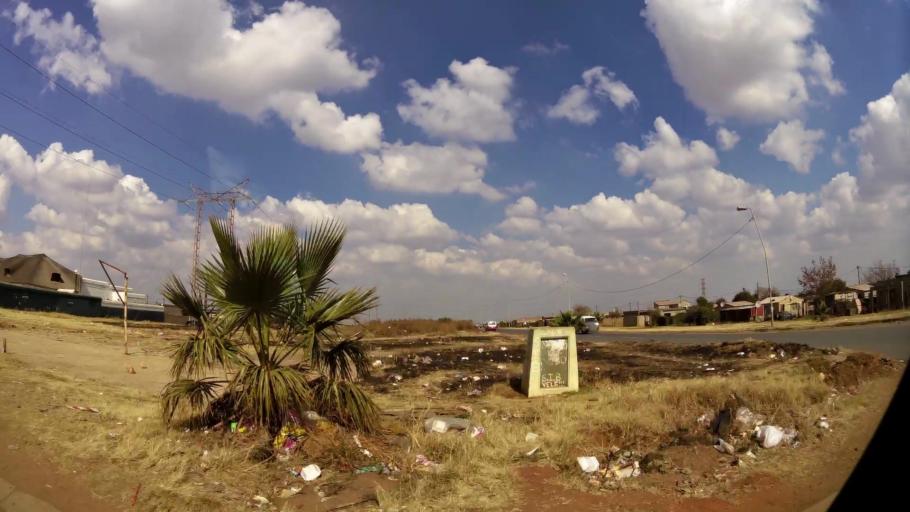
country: ZA
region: Gauteng
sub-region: City of Johannesburg Metropolitan Municipality
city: Roodepoort
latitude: -26.1902
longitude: 27.8563
